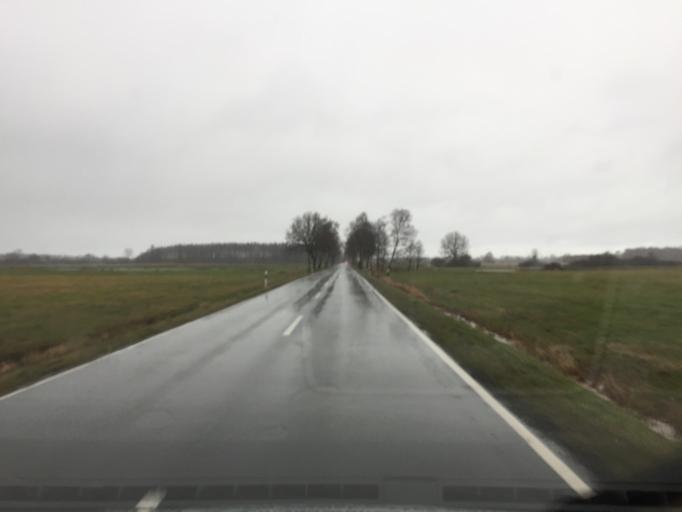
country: DE
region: Lower Saxony
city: Maasen
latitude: 52.6315
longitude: 8.8871
